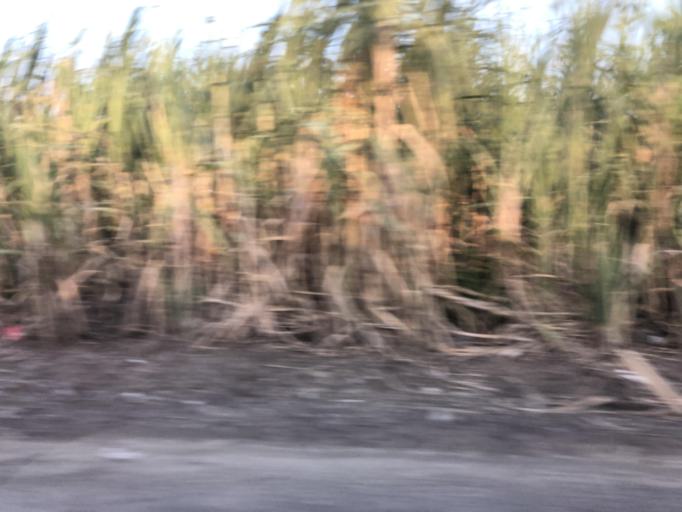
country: TW
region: Taiwan
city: Xinying
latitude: 23.1615
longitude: 120.2709
